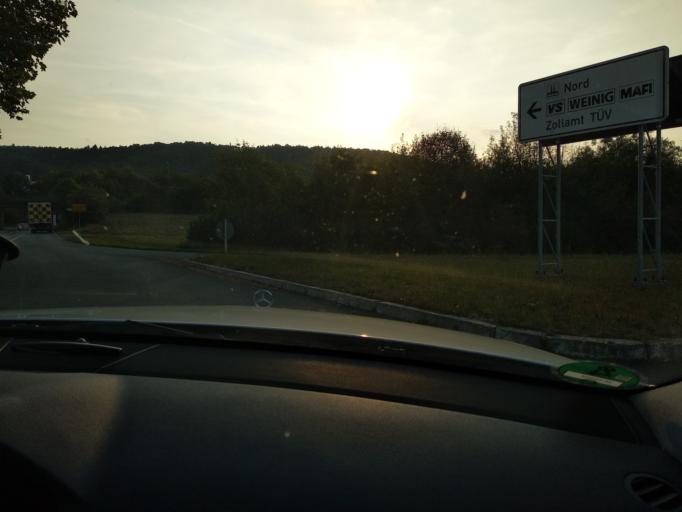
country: DE
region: Baden-Wuerttemberg
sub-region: Regierungsbezirk Stuttgart
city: Tauberbischofsheim
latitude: 49.6392
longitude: 9.6521
